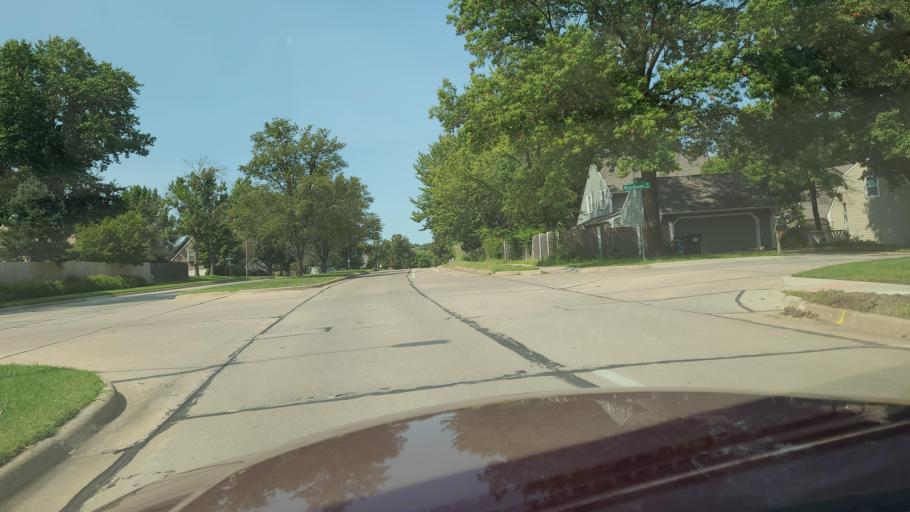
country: US
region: Kansas
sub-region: Douglas County
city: Lawrence
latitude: 38.9844
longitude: -95.2748
